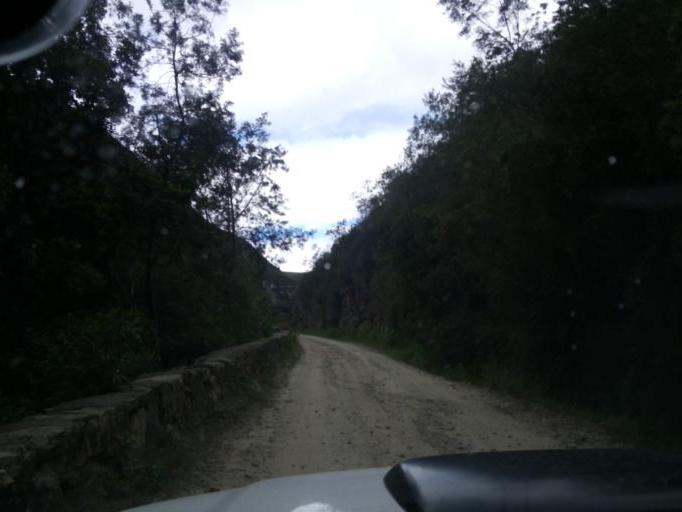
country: ZA
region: Western Cape
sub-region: Eden District Municipality
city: George
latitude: -33.8992
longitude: 22.4152
